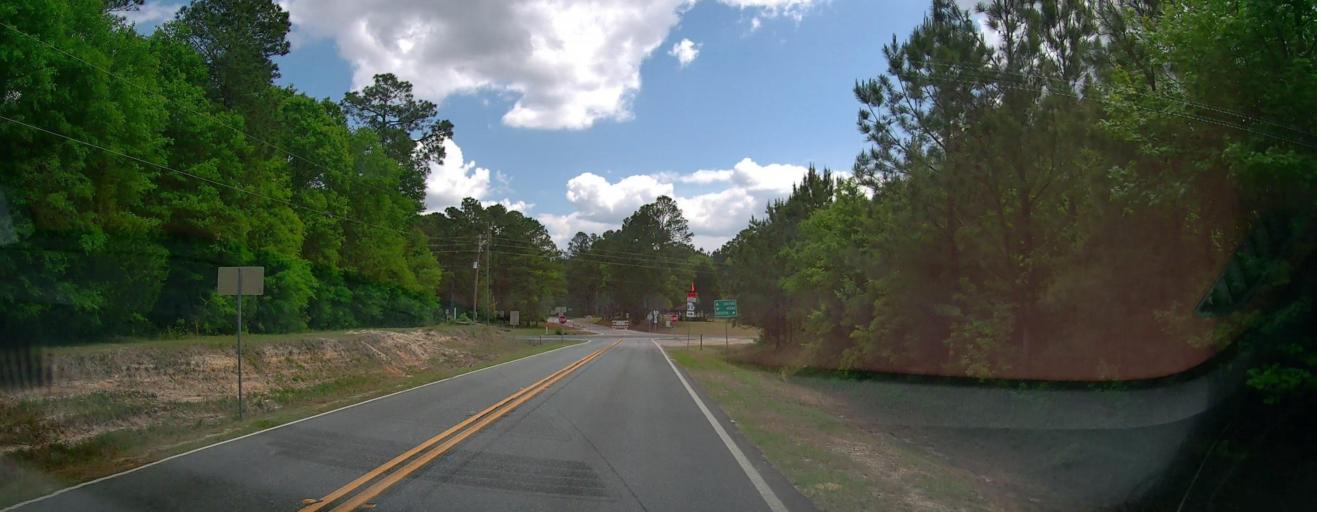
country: US
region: Georgia
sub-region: Treutlen County
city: Soperton
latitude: 32.4831
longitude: -82.5997
